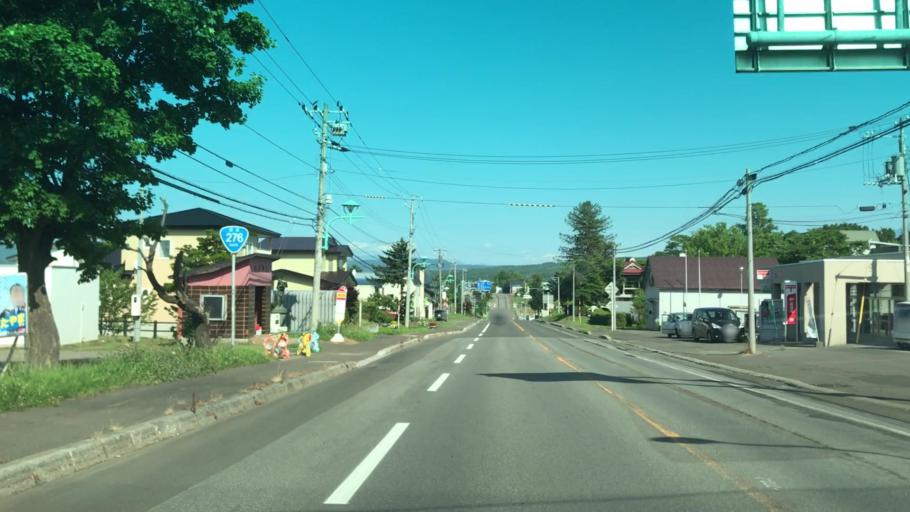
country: JP
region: Hokkaido
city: Iwanai
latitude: 42.9813
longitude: 140.5741
